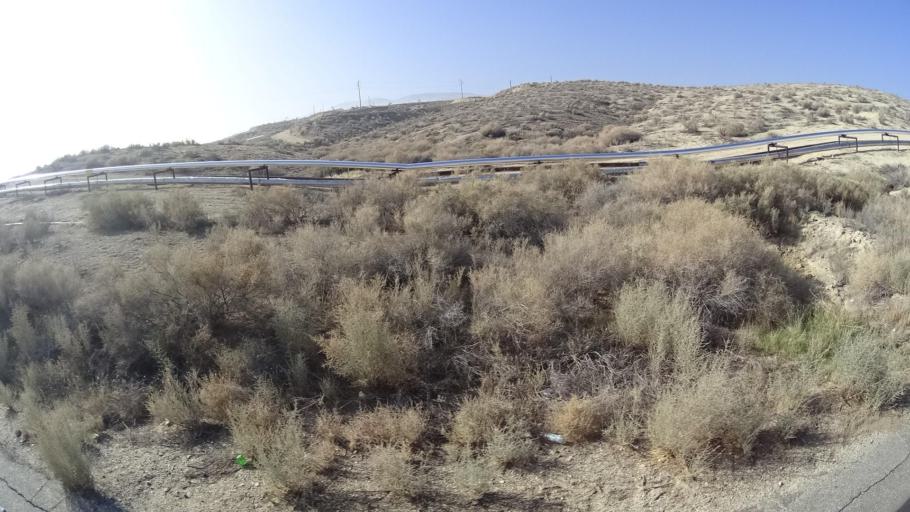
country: US
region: California
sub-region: Kern County
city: Taft Heights
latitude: 35.1457
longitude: -119.5134
